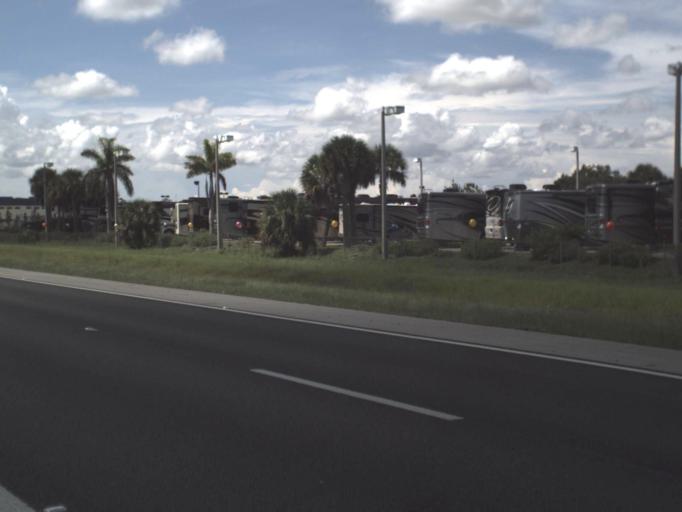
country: US
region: Florida
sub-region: Lee County
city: Tice
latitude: 26.6793
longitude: -81.7988
